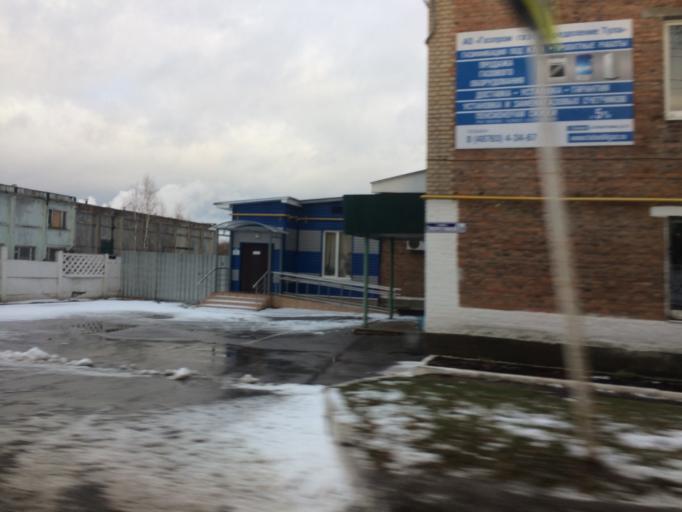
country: RU
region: Tula
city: Suvorov
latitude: 54.1255
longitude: 36.4855
